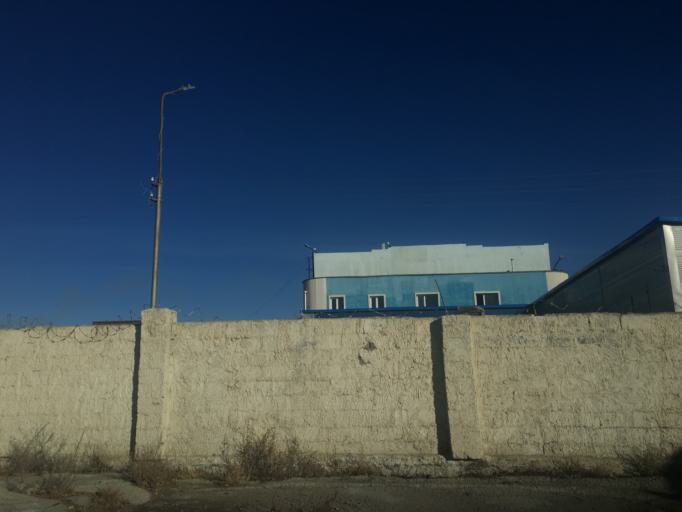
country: MN
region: Ulaanbaatar
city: Ulaanbaatar
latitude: 47.8981
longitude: 106.7956
